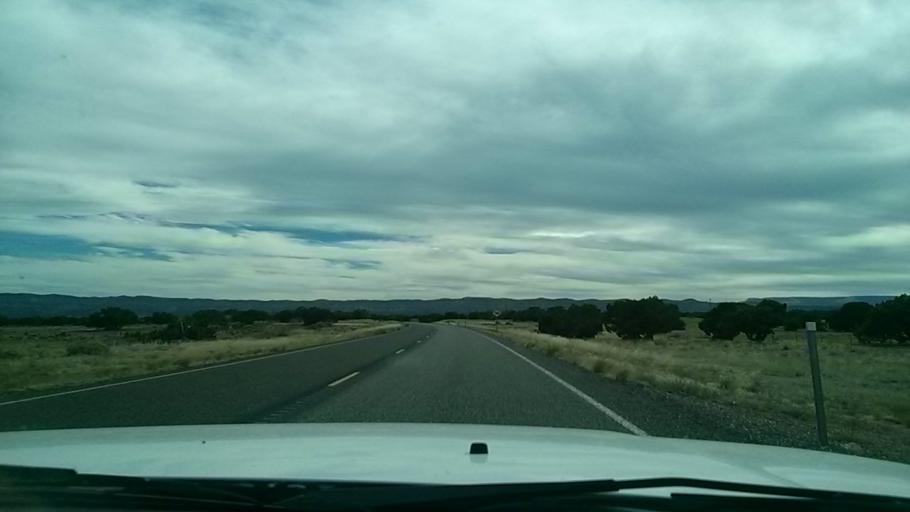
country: US
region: Utah
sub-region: Wayne County
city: Loa
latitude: 37.7475
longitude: -111.4940
